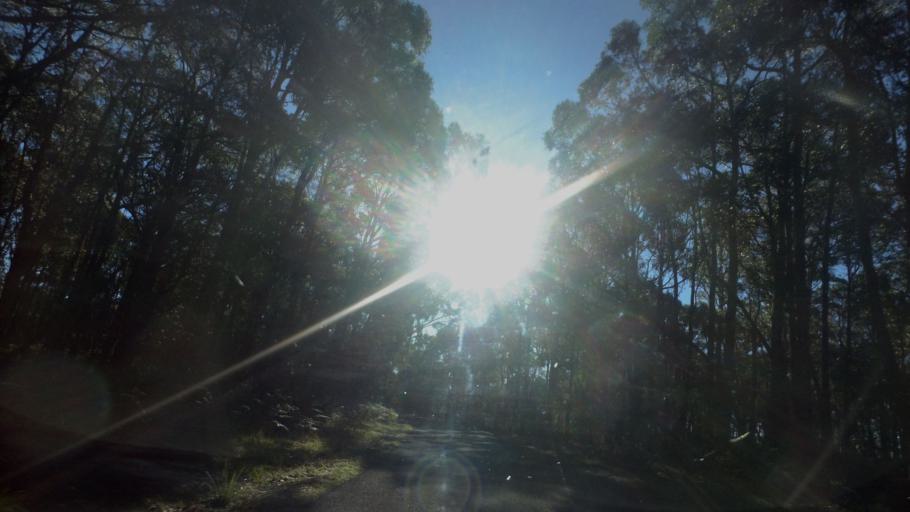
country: AU
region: Victoria
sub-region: Mount Alexander
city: Castlemaine
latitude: -37.3286
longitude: 144.3188
